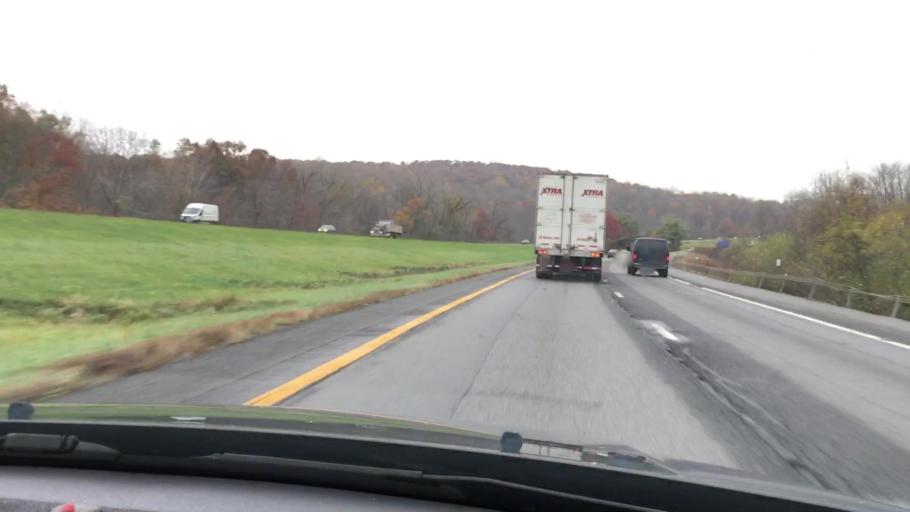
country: US
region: New York
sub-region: Putnam County
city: Lake Carmel
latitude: 41.4885
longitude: -73.6617
